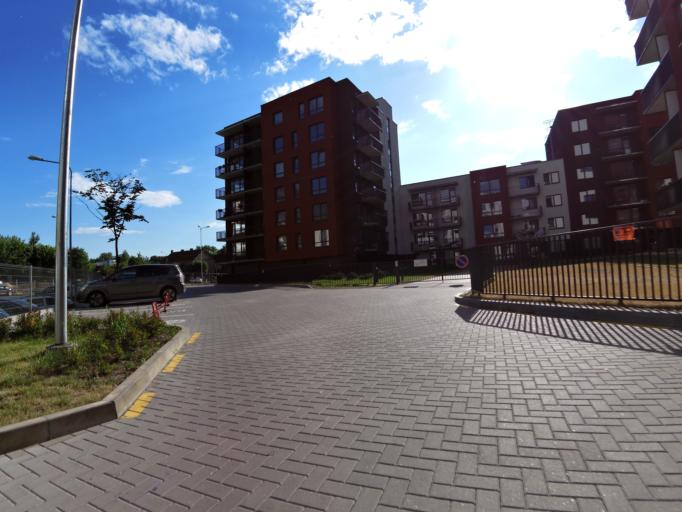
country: LT
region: Vilnius County
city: Naujamiestis
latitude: 54.6720
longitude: 25.2742
